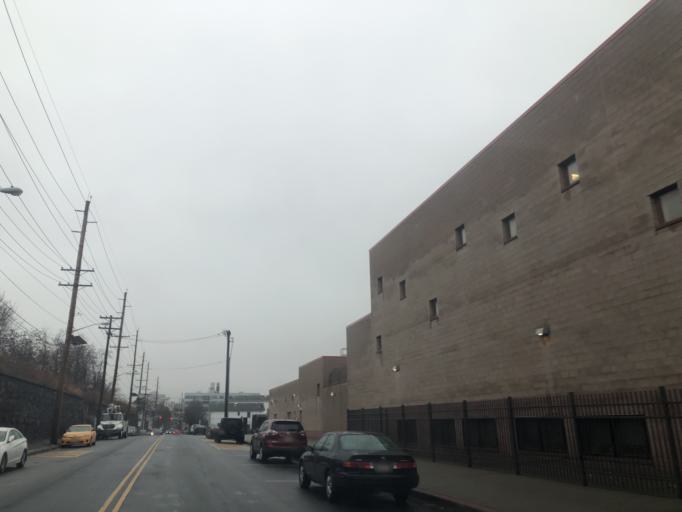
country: US
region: New Jersey
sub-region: Hudson County
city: Jersey City
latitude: 40.7396
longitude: -74.0564
